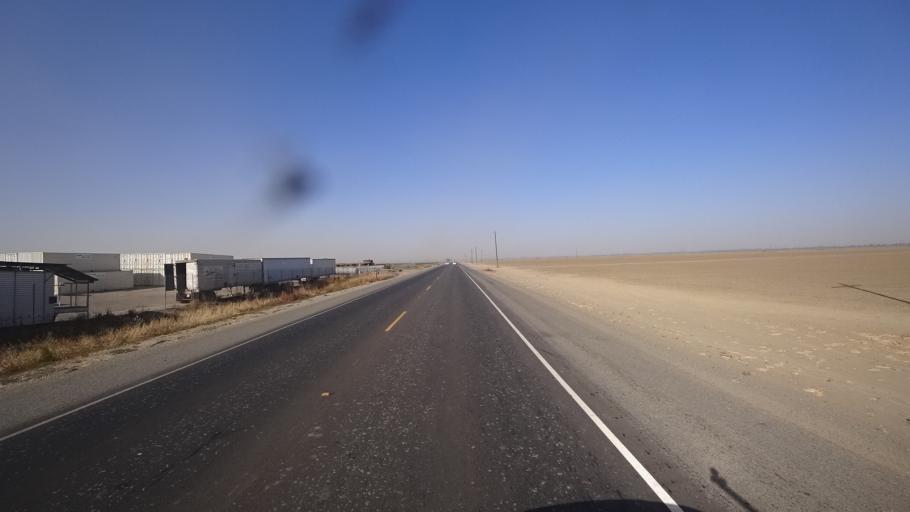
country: US
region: California
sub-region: Yolo County
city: Woodland
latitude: 38.7536
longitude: -121.7292
